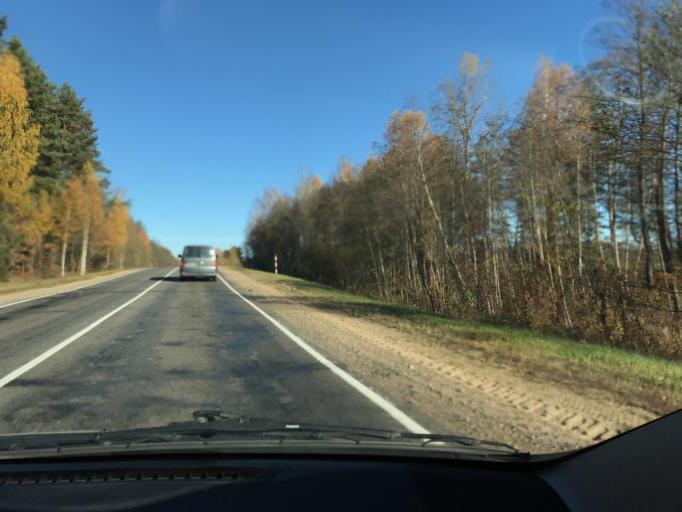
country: BY
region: Vitebsk
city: Polatsk
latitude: 55.3231
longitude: 28.7816
